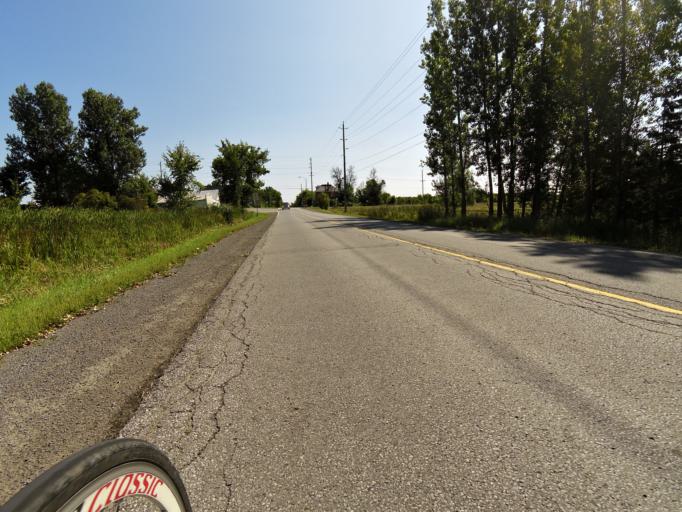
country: CA
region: Ontario
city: Arnprior
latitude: 45.4549
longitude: -76.0901
